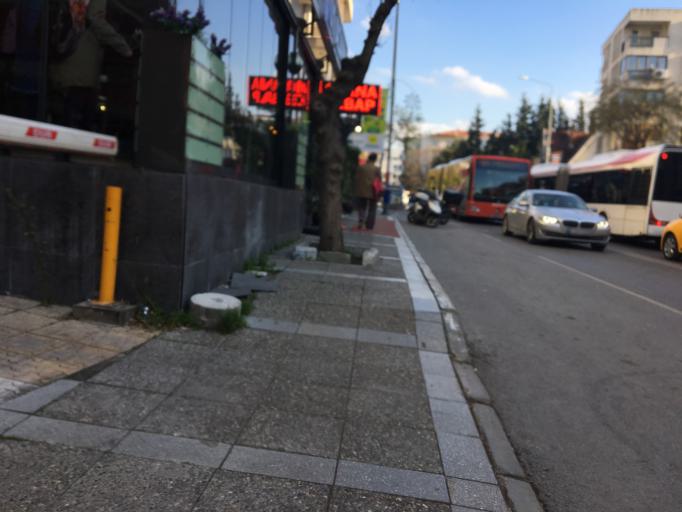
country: TR
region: Izmir
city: Buca
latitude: 38.3896
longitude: 27.1680
